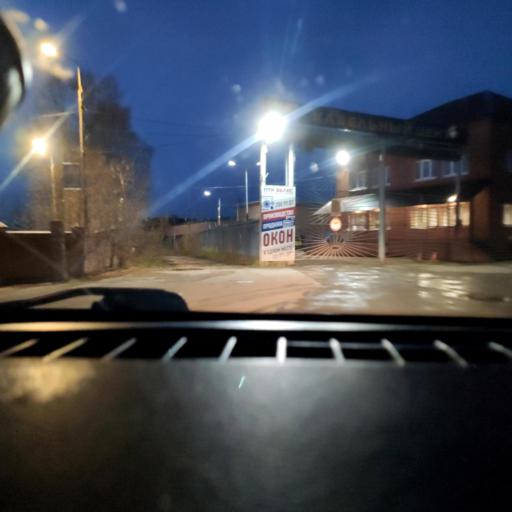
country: RU
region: Perm
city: Kondratovo
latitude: 58.0221
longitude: 56.1642
